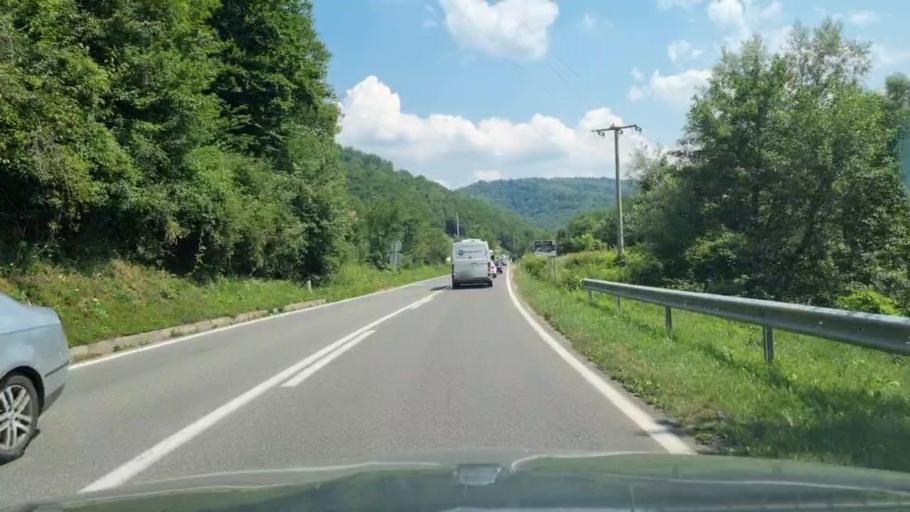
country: BA
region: Federation of Bosnia and Herzegovina
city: Gornje Zivinice
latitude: 44.3898
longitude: 18.6615
